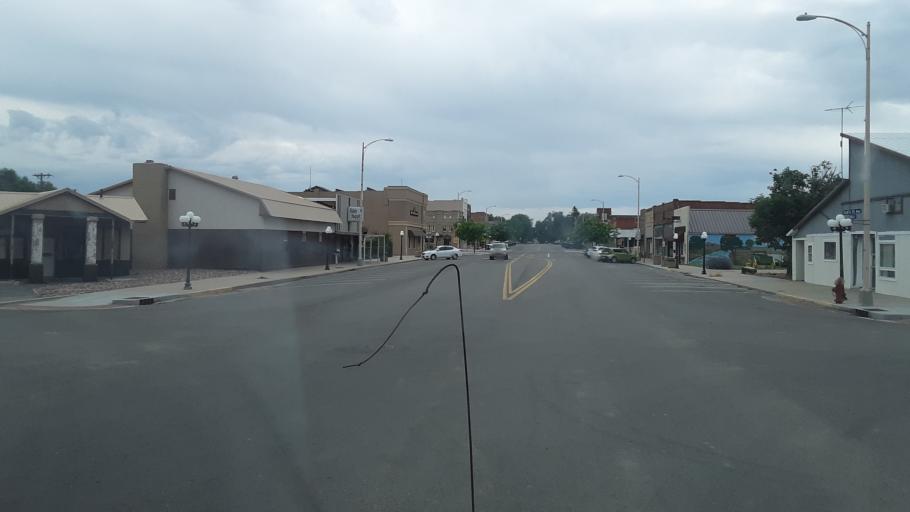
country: US
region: Colorado
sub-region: Otero County
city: Fowler
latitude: 38.1320
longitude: -104.0235
